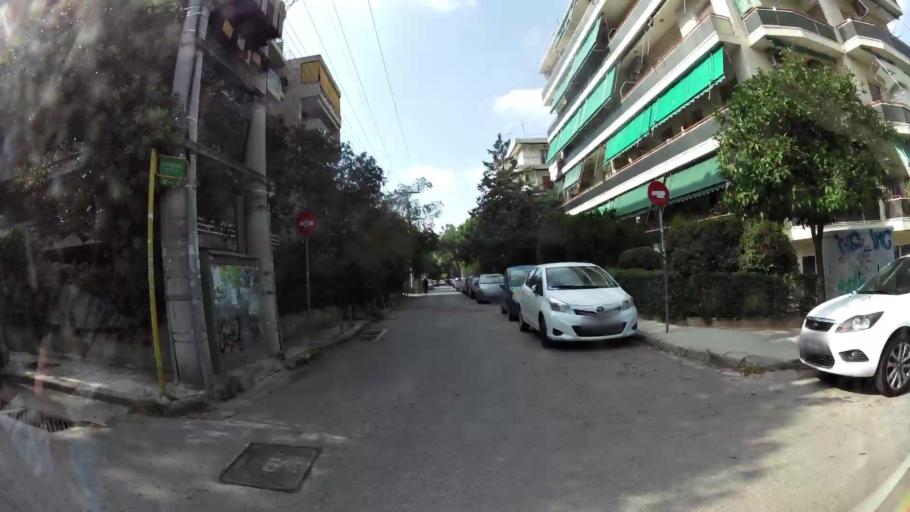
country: GR
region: Attica
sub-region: Nomarchia Athinas
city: Cholargos
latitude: 37.9936
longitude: 23.8035
